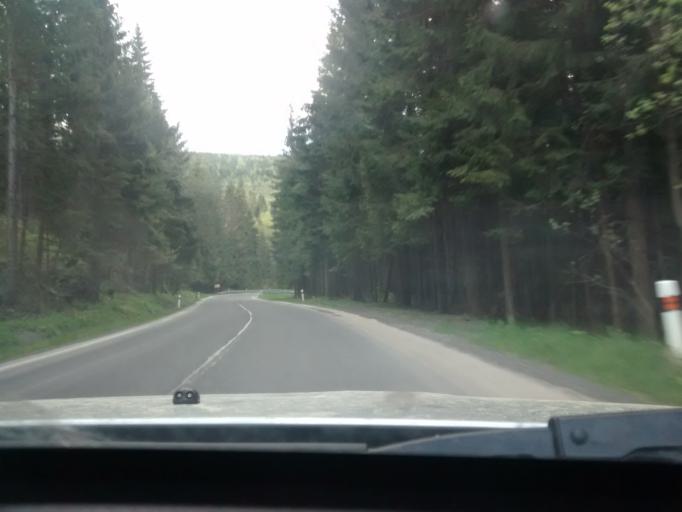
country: SK
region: Presovsky
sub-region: Okres Poprad
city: Zdiar
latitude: 49.2786
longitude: 20.2074
